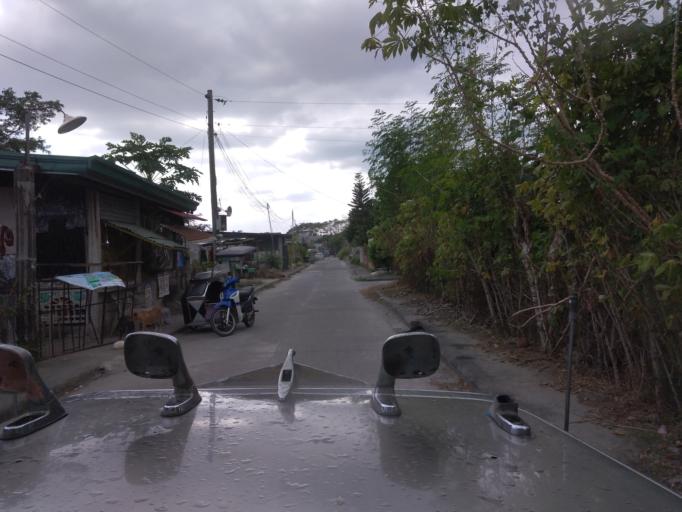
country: PH
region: Central Luzon
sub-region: Province of Pampanga
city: Pandacaqui
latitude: 15.1855
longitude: 120.6488
